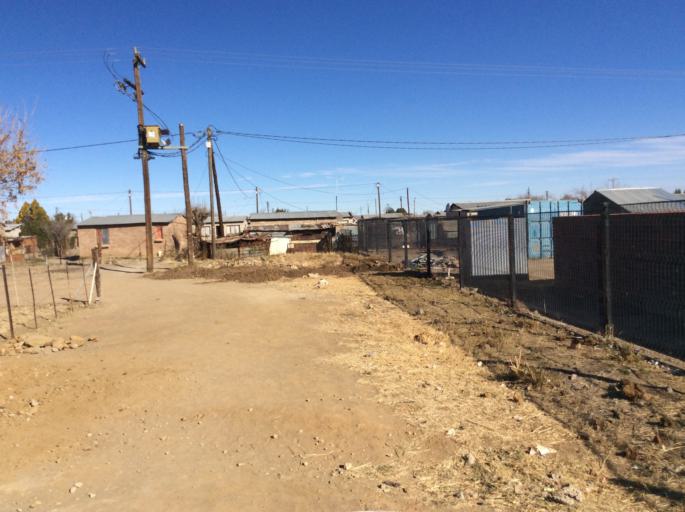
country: ZA
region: Orange Free State
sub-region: Lejweleputswa District Municipality
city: Brandfort
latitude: -28.7329
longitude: 26.1075
